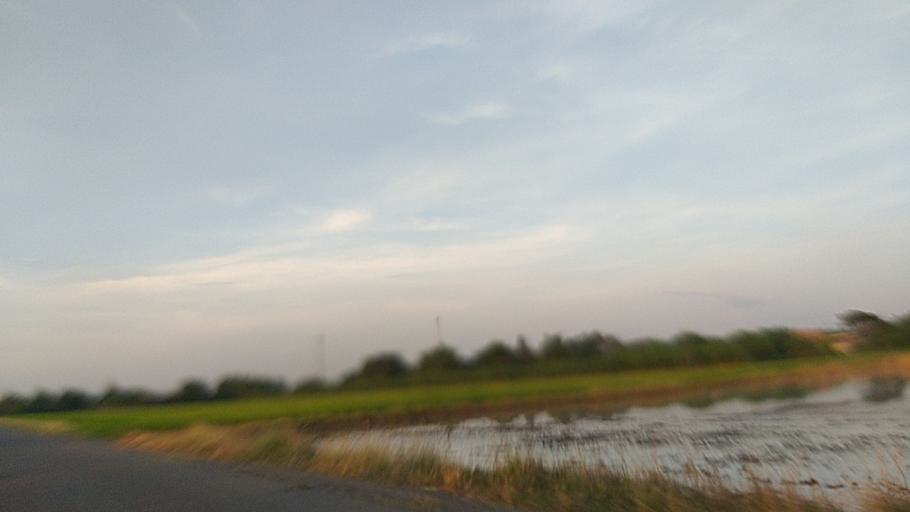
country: TH
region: Pathum Thani
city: Nong Suea
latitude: 14.0631
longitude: 100.8678
